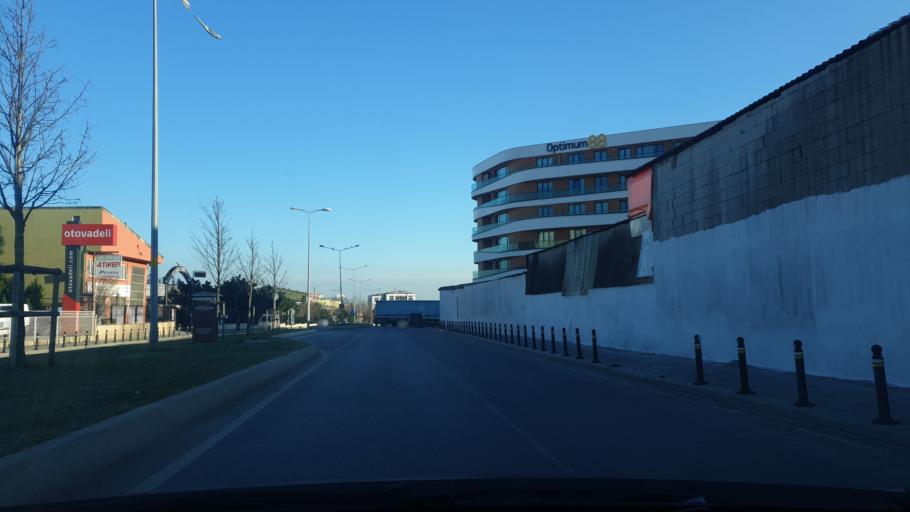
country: TR
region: Istanbul
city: Pendik
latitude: 40.8967
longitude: 29.2601
